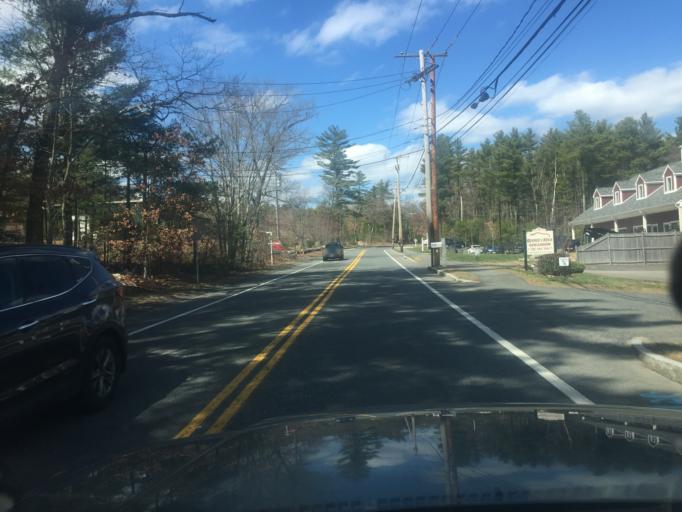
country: US
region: Massachusetts
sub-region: Norfolk County
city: Norfolk
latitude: 42.0927
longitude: -71.3016
